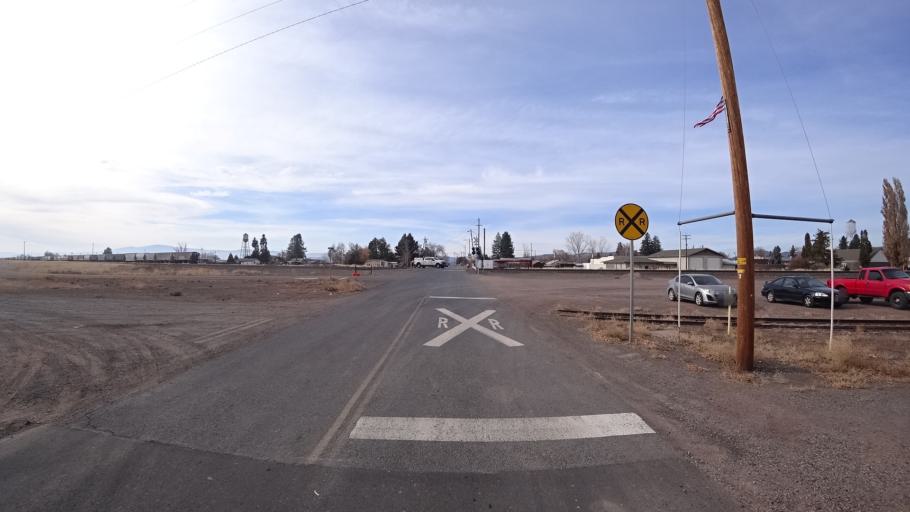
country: US
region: Oregon
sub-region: Klamath County
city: Klamath Falls
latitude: 41.9626
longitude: -121.9168
